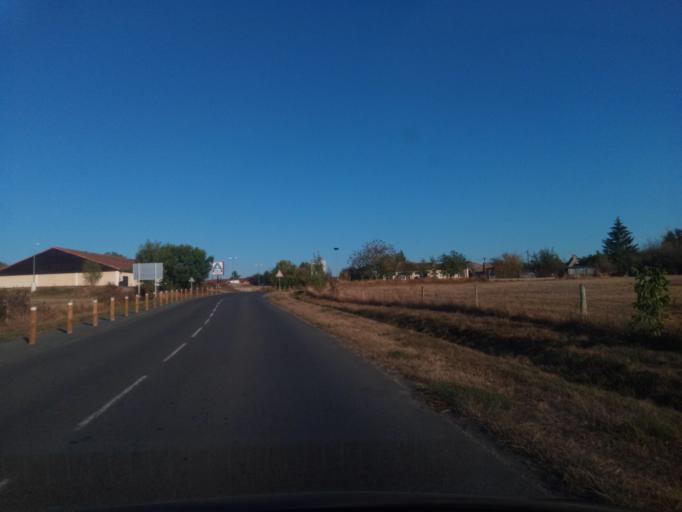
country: FR
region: Poitou-Charentes
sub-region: Departement de la Vienne
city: Montmorillon
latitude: 46.4183
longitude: 0.8614
